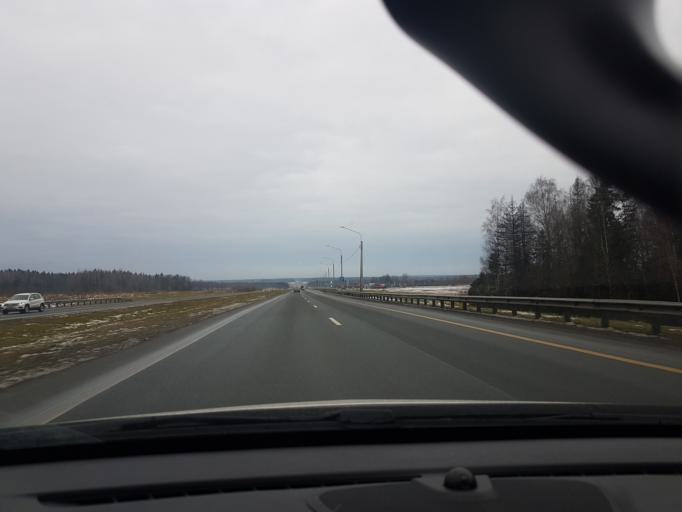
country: RU
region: Moskovskaya
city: Sychevo
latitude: 55.9888
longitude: 36.2796
